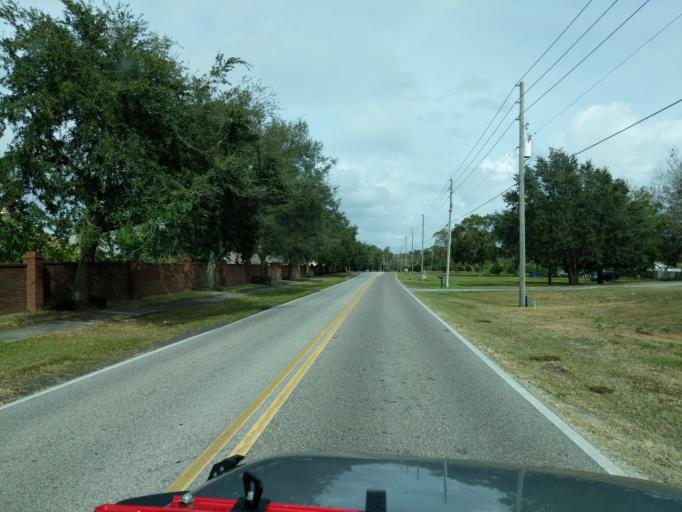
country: US
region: Florida
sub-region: Orange County
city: Ocoee
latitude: 28.5843
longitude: -81.5609
